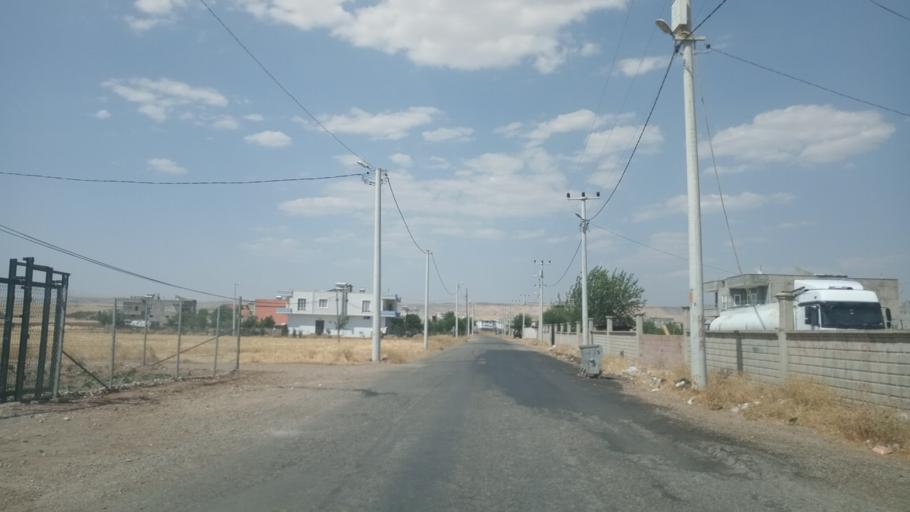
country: TR
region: Batman
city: Binatli
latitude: 37.8401
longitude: 41.2100
